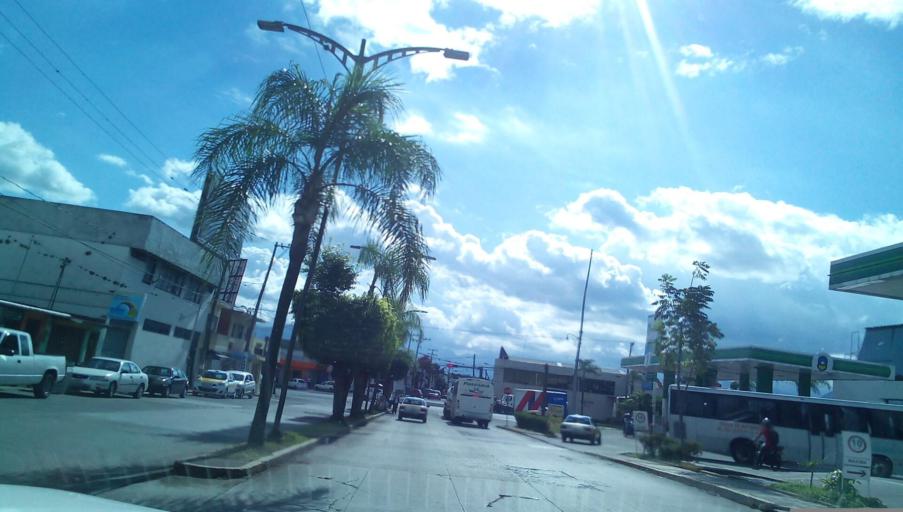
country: MX
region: Veracruz
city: Cordoba
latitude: 18.8811
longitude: -96.9206
